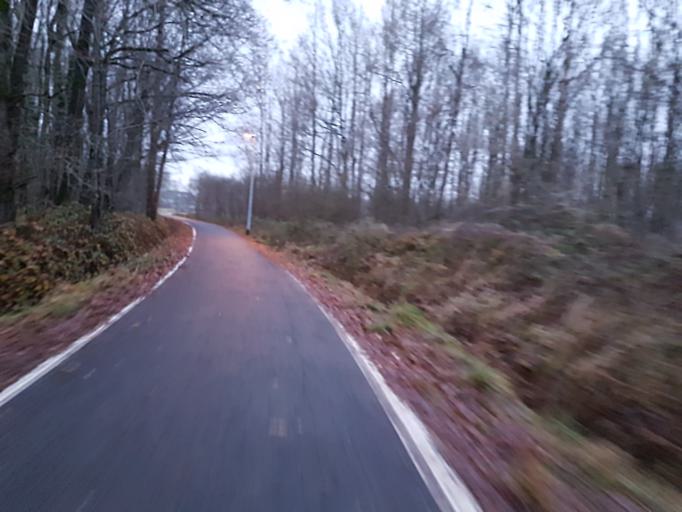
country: BE
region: Flanders
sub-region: Provincie Vlaams-Brabant
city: Rotselaar
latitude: 50.9659
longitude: 4.7198
